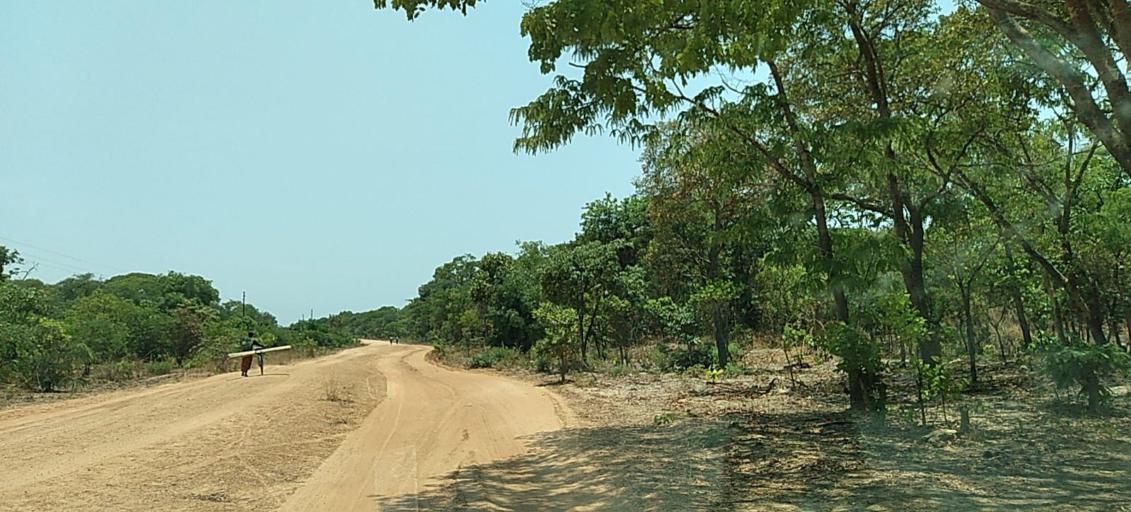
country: ZM
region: Copperbelt
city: Mpongwe
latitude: -13.8042
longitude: 27.8581
